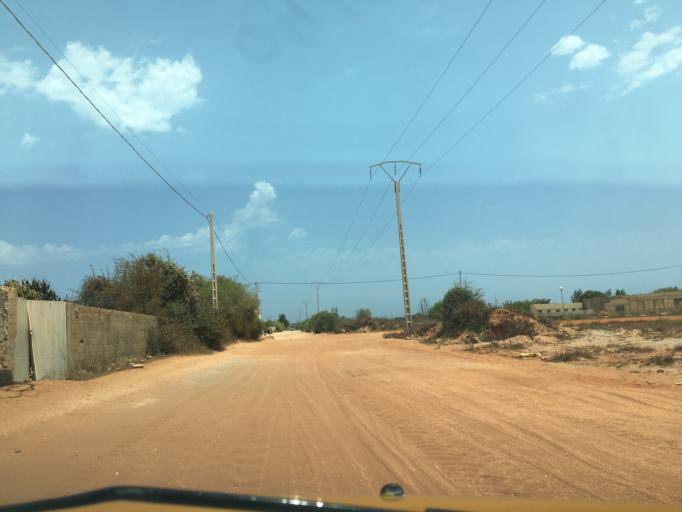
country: SN
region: Thies
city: Thies
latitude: 14.8116
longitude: -17.1916
